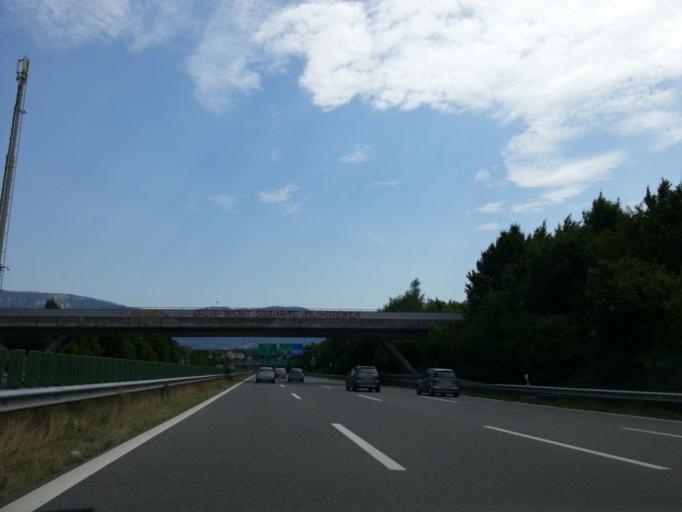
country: CH
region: Geneva
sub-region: Geneva
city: Confignon
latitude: 46.1701
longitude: 6.0935
